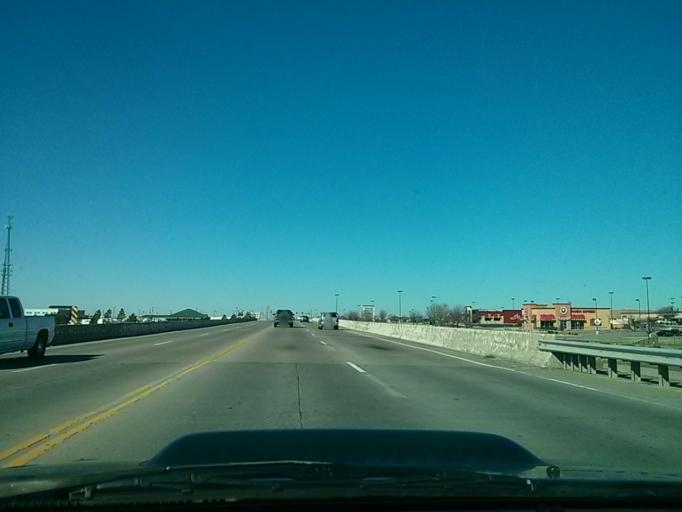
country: US
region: Oklahoma
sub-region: Tulsa County
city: Owasso
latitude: 36.2933
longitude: -95.8329
